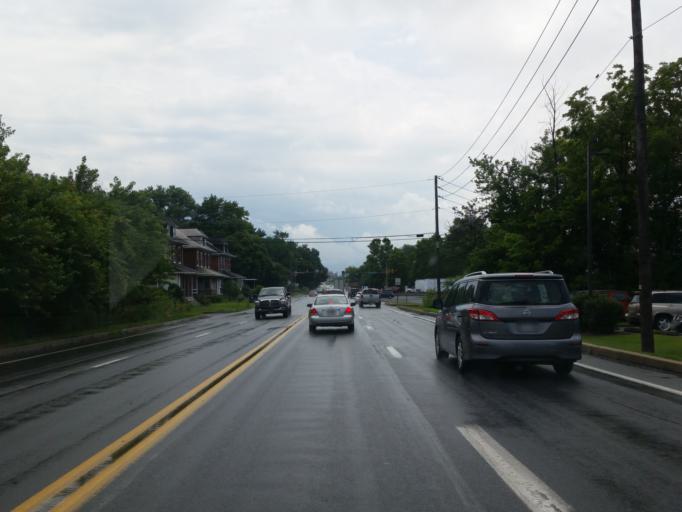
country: US
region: Pennsylvania
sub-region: Lancaster County
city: Lancaster
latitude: 40.0642
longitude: -76.3145
